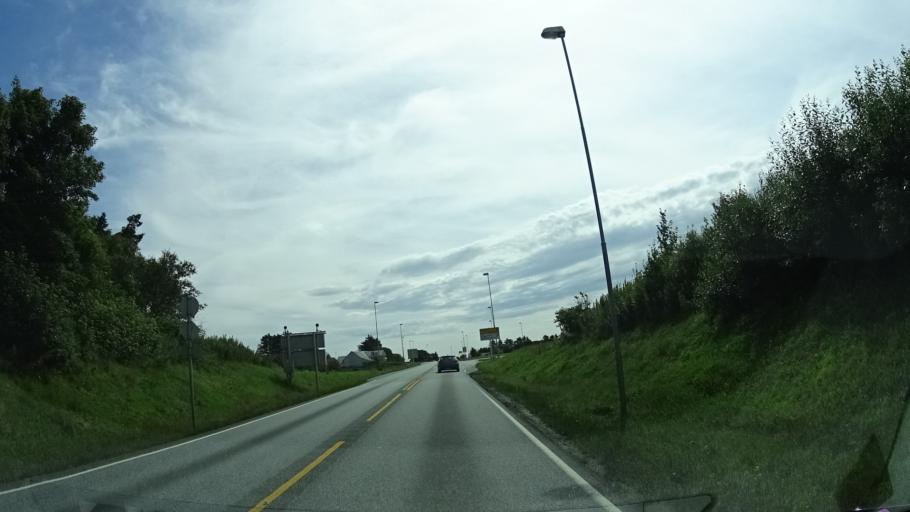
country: NO
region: Rogaland
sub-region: Randaberg
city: Randaberg
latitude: 59.0100
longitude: 5.6378
